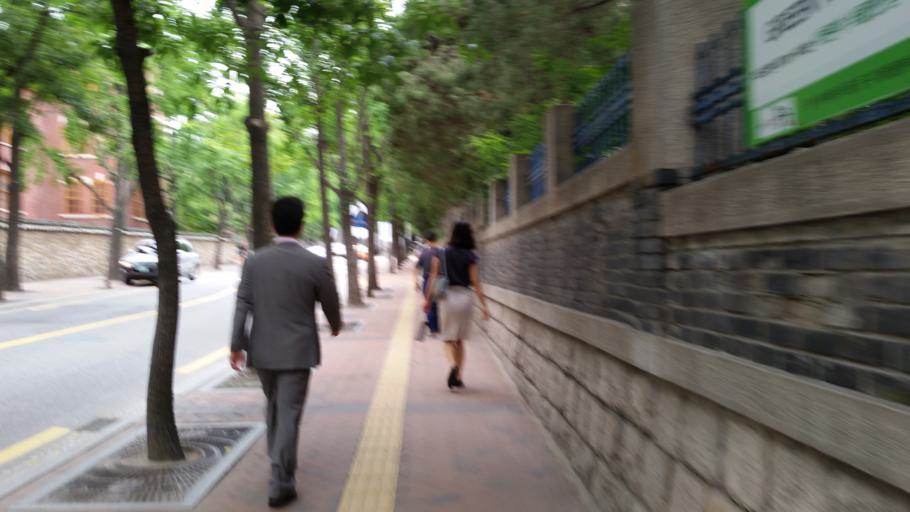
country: KR
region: Seoul
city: Seoul
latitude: 37.5662
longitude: 126.9719
